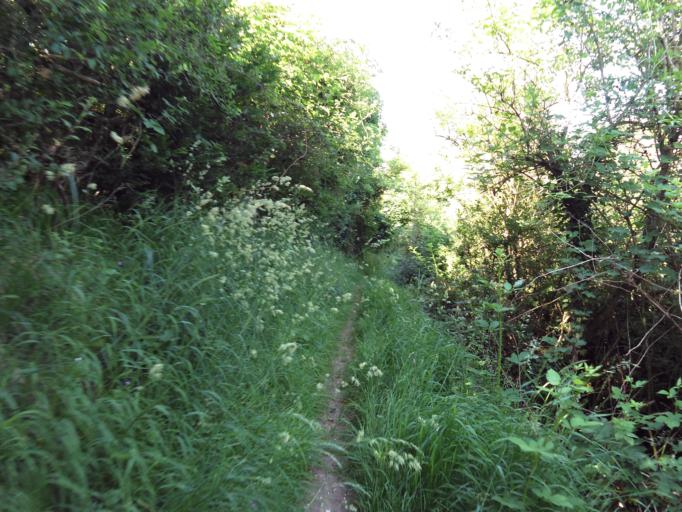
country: DE
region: Rheinland-Pfalz
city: Mertesheim
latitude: 49.5688
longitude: 8.1281
